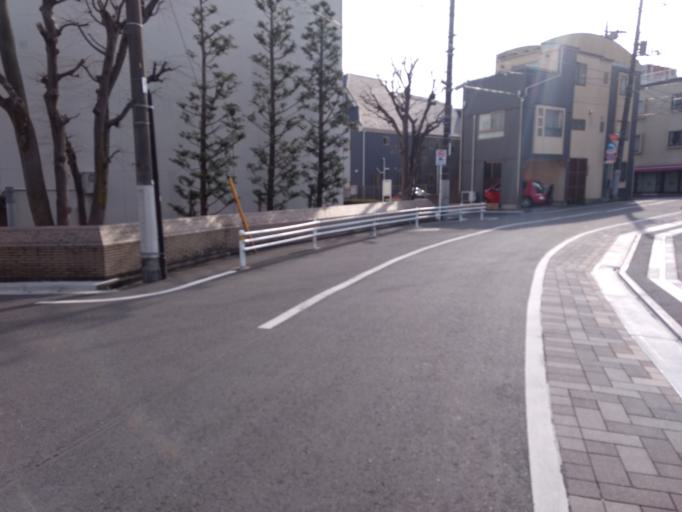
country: JP
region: Tokyo
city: Musashino
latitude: 35.6982
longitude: 139.6242
